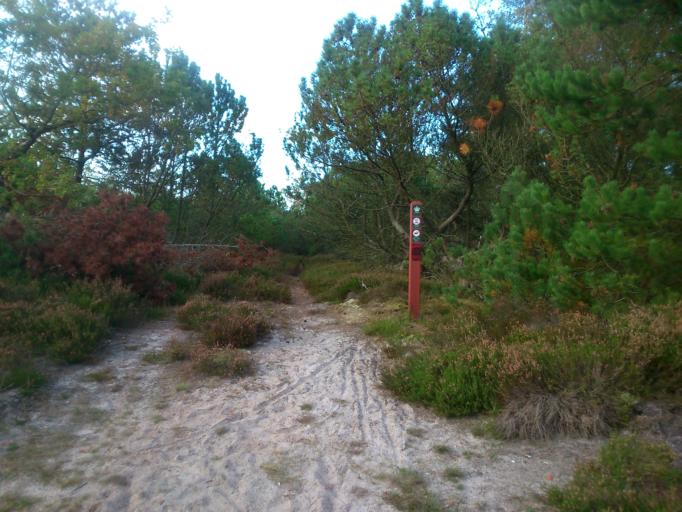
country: DK
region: South Denmark
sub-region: Varde Kommune
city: Oksbol
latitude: 55.6846
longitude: 8.1726
